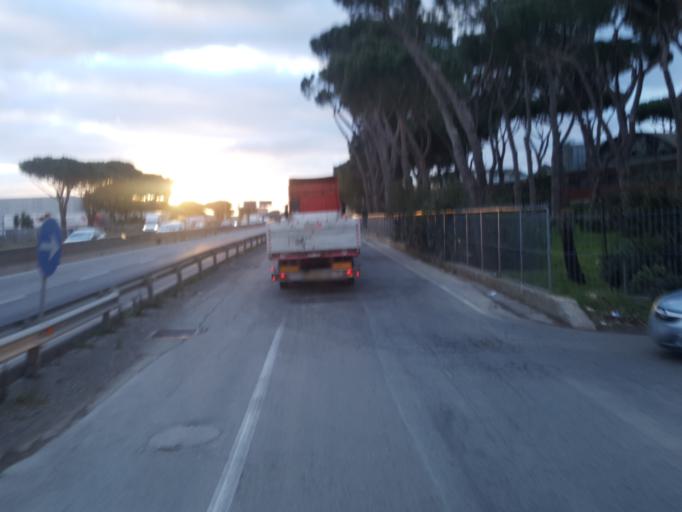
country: IT
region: Latium
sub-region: Citta metropolitana di Roma Capitale
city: Area Produttiva
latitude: 41.6896
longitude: 12.4848
